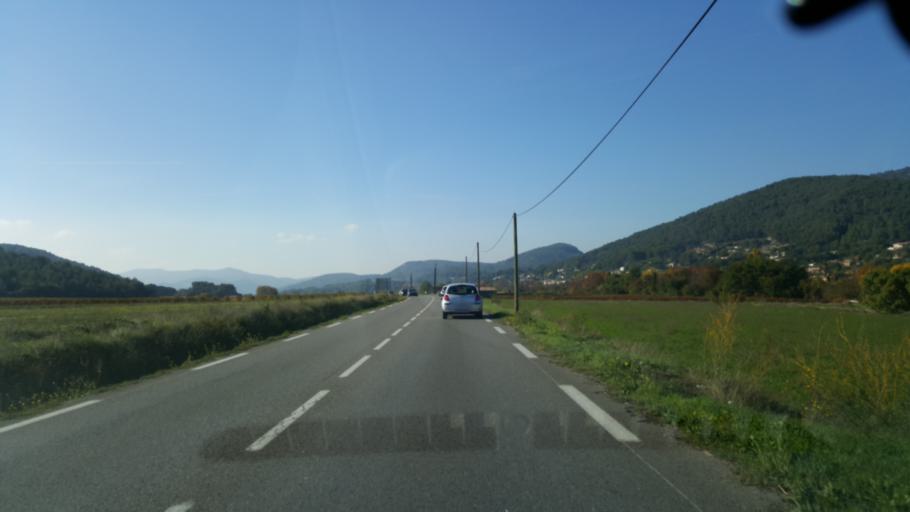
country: FR
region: Provence-Alpes-Cote d'Azur
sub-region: Departement du Var
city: Saint-Zacharie
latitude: 43.3786
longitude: 5.6930
